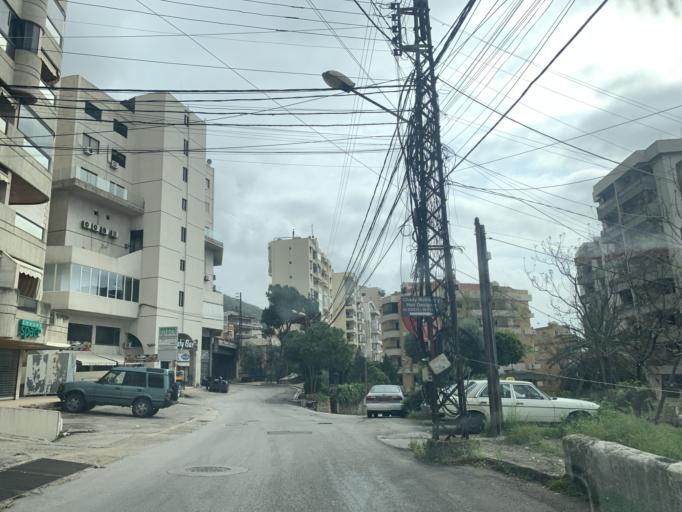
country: LB
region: Mont-Liban
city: Djounie
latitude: 33.9904
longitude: 35.6441
